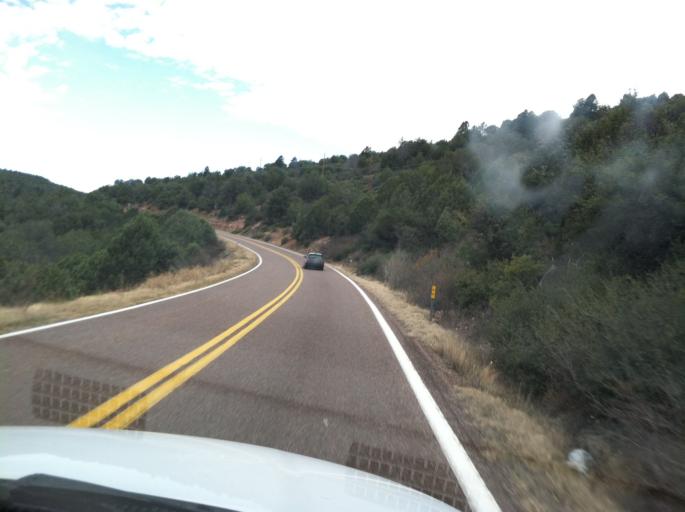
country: US
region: Arizona
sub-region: Gila County
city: Pine
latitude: 34.3167
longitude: -111.3900
